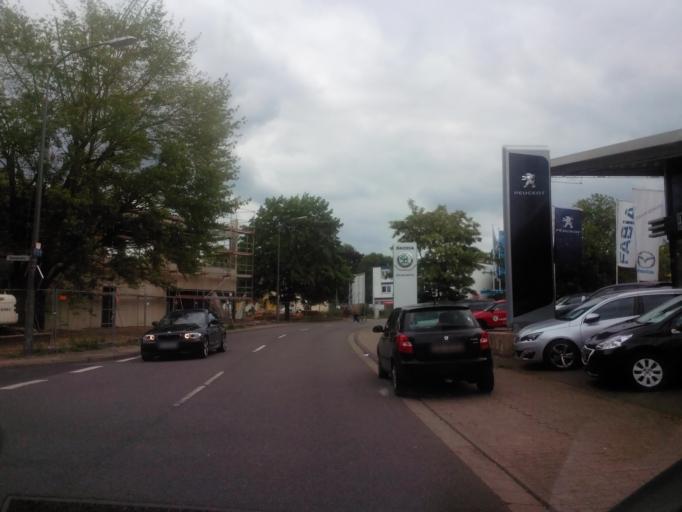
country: DE
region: Saarland
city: Saarlouis
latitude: 49.3060
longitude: 6.7396
